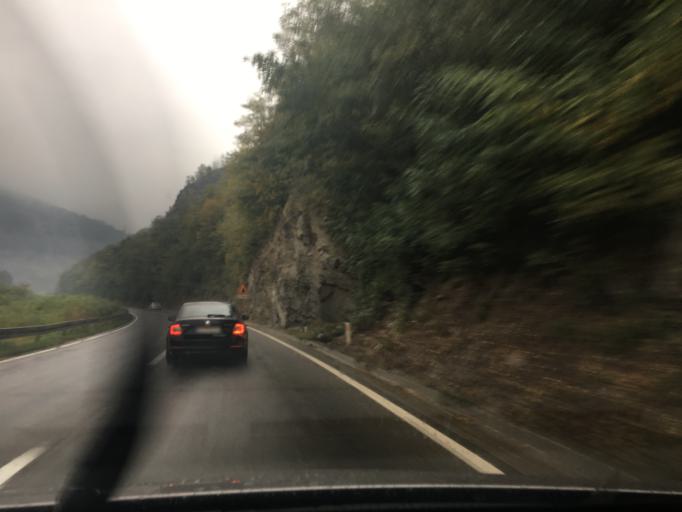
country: RS
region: Central Serbia
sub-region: Pcinjski Okrug
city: Vladicin Han
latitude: 42.7321
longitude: 22.0656
